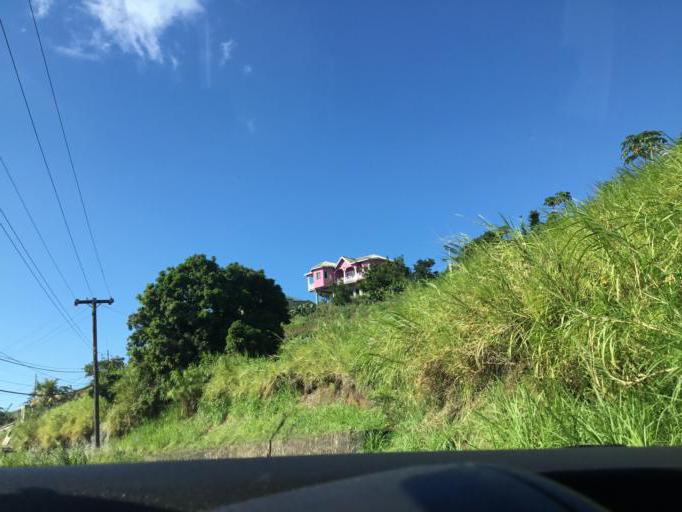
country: VC
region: Saint David
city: Chateaubelair
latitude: 13.2747
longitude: -61.2464
